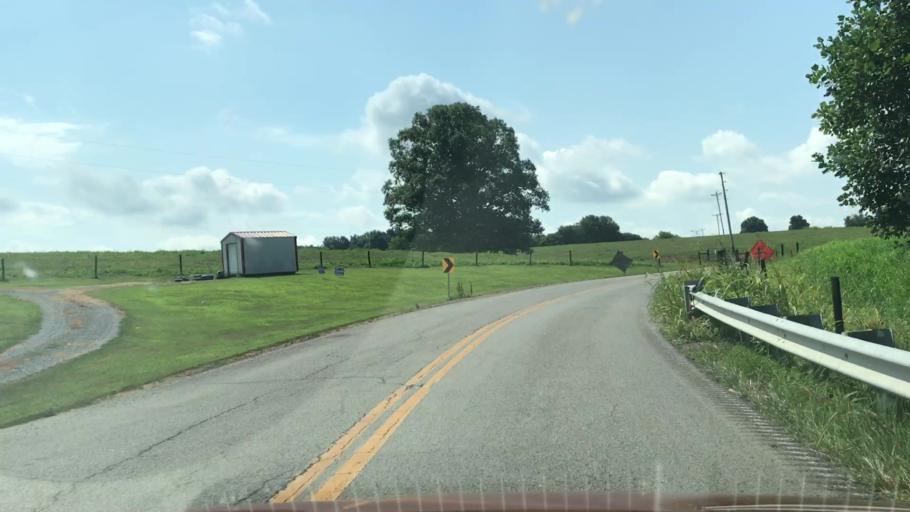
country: US
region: Kentucky
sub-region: Barren County
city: Glasgow
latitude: 36.8542
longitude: -85.8385
